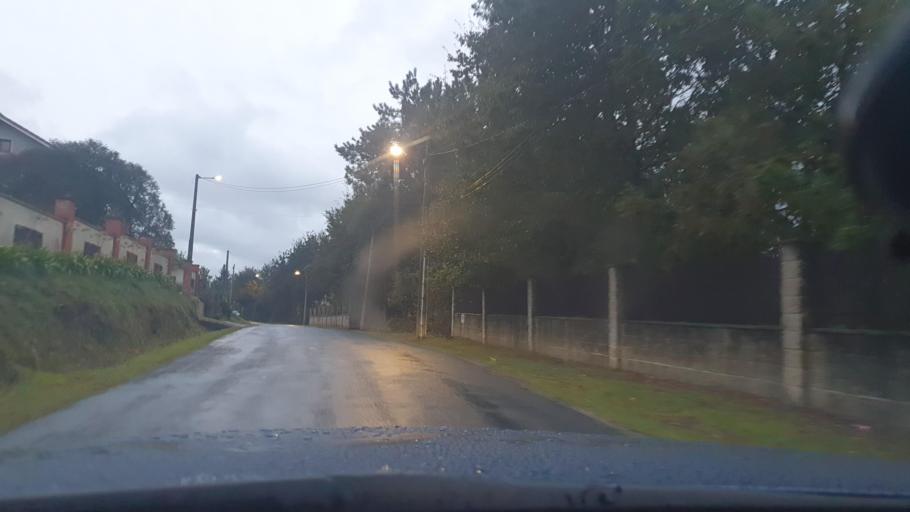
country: ES
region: Galicia
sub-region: Provincia da Coruna
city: Santiago de Compostela
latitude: 42.8551
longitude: -8.5889
